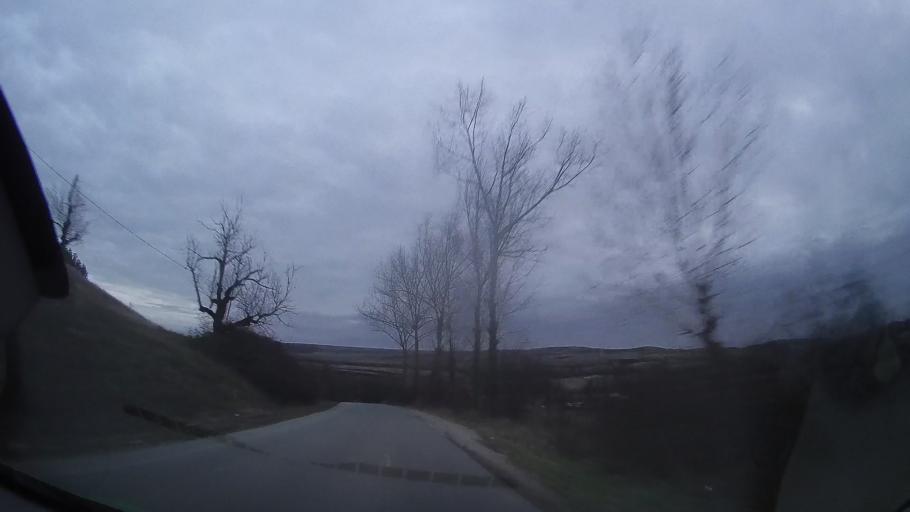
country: RO
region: Cluj
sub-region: Comuna Caianu
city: Caianu
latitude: 46.8039
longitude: 23.9302
